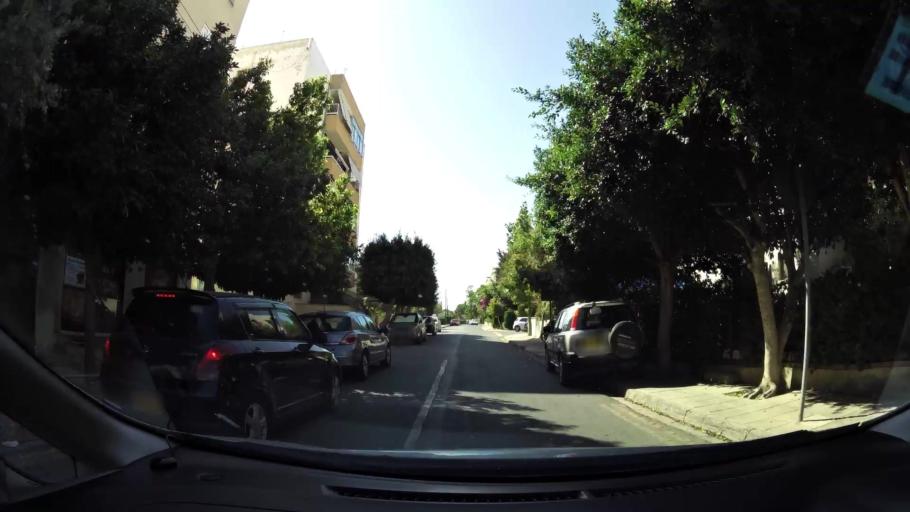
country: CY
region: Lefkosia
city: Nicosia
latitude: 35.1470
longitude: 33.3525
